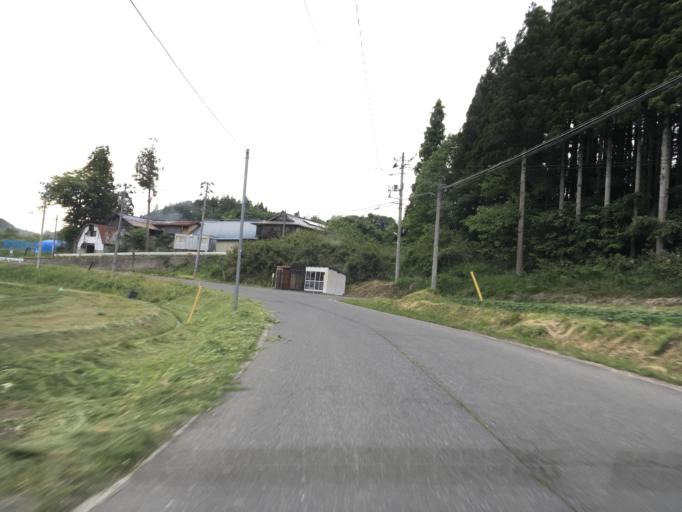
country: JP
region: Iwate
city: Mizusawa
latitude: 39.1740
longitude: 141.2970
